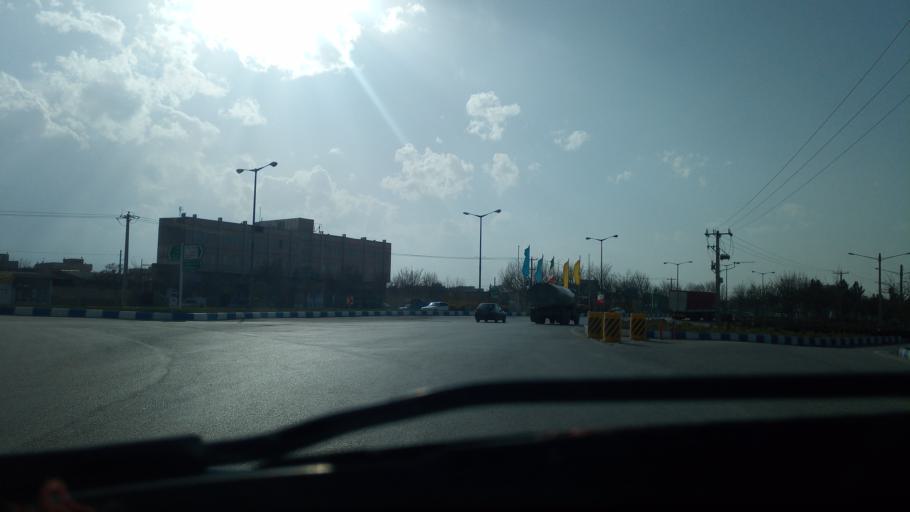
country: IR
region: Razavi Khorasan
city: Quchan
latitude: 37.0917
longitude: 58.5128
